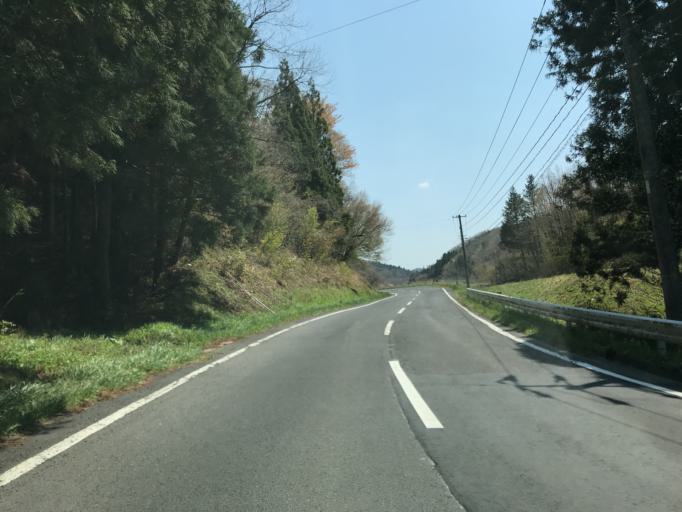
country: JP
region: Fukushima
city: Ishikawa
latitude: 37.0588
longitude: 140.4582
